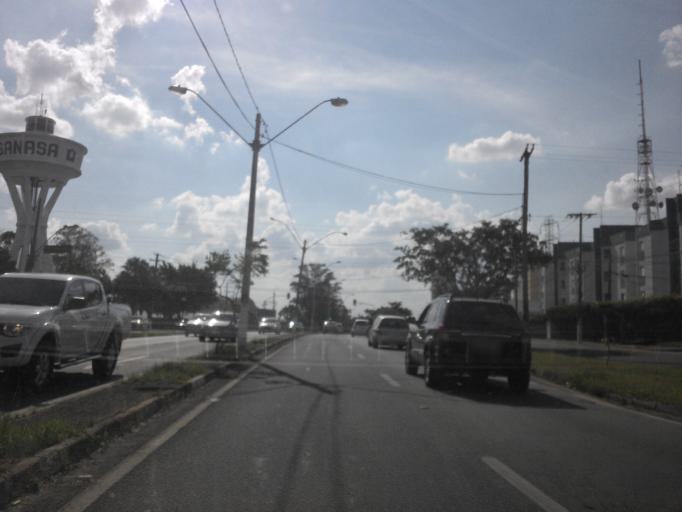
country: BR
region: Sao Paulo
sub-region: Valinhos
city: Valinhos
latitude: -22.9433
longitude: -47.0320
